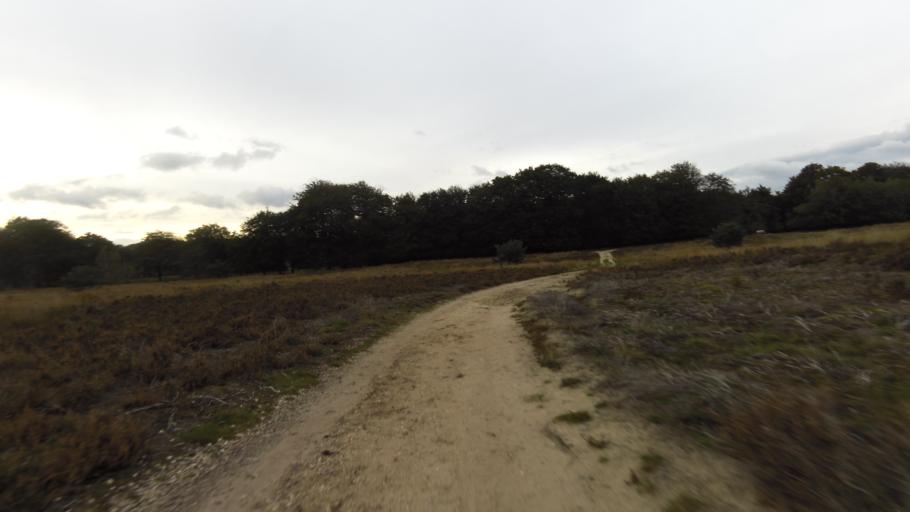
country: NL
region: Gelderland
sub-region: Gemeente Ede
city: Otterlo
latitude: 52.1718
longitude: 5.8540
